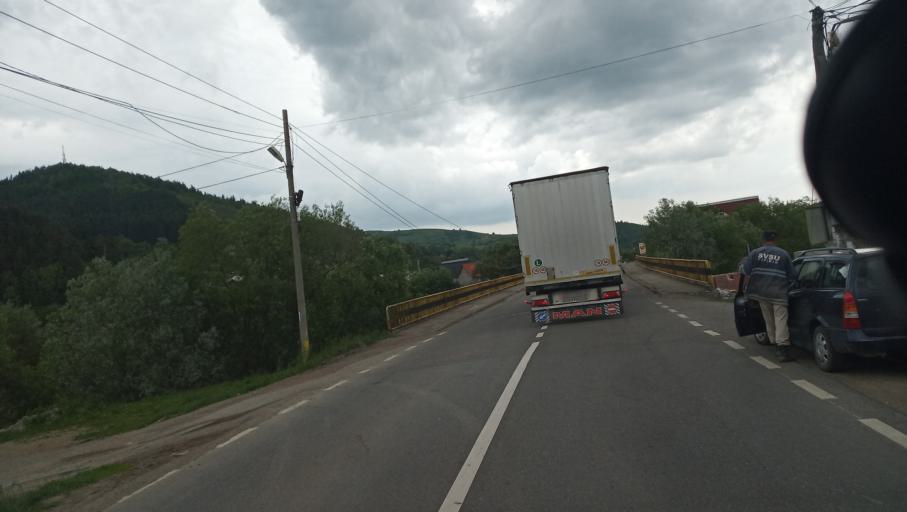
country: RO
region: Neamt
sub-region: Comuna Pipirig
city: Dolhesti
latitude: 47.2292
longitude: 26.0847
